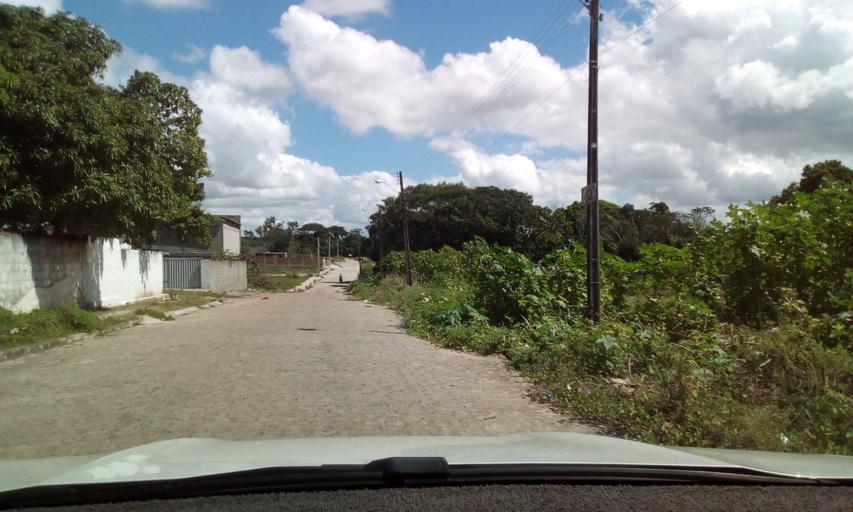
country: BR
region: Paraiba
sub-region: Joao Pessoa
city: Joao Pessoa
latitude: -7.1738
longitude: -34.8211
